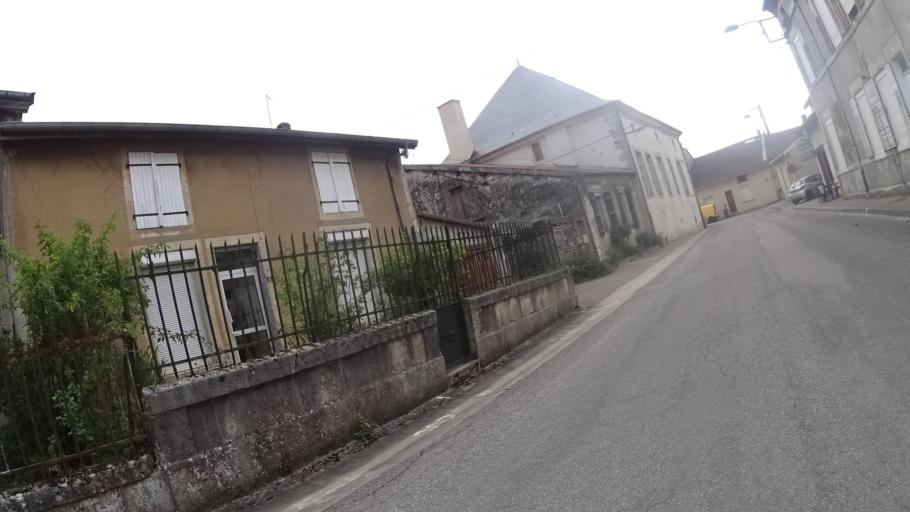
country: FR
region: Lorraine
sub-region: Departement de la Meuse
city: Tronville-en-Barrois
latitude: 48.7205
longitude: 5.2797
